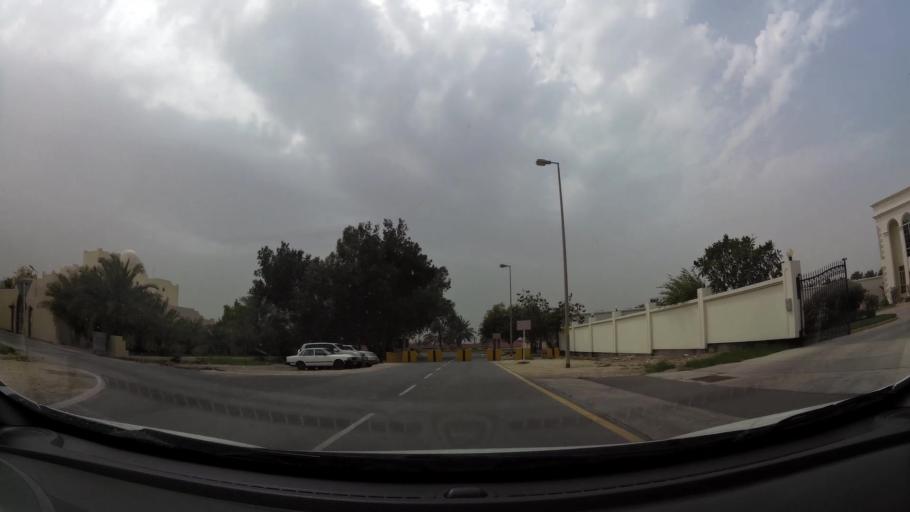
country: BH
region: Central Governorate
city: Madinat Hamad
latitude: 26.1188
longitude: 50.5284
